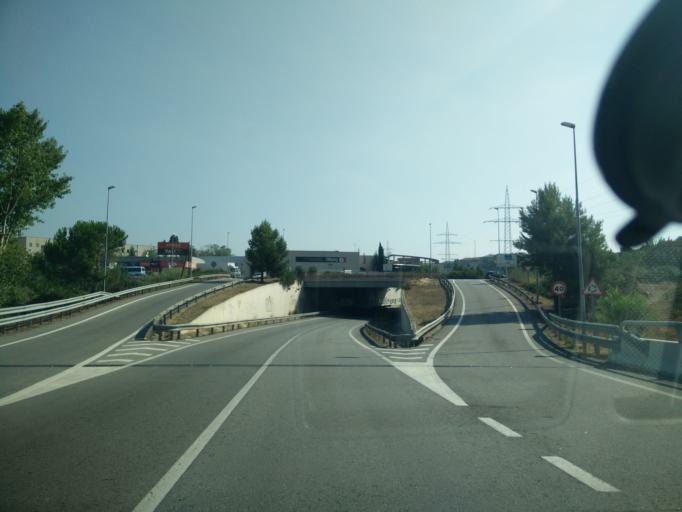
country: ES
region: Catalonia
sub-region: Provincia de Barcelona
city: Terrassa
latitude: 41.5334
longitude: 2.0333
